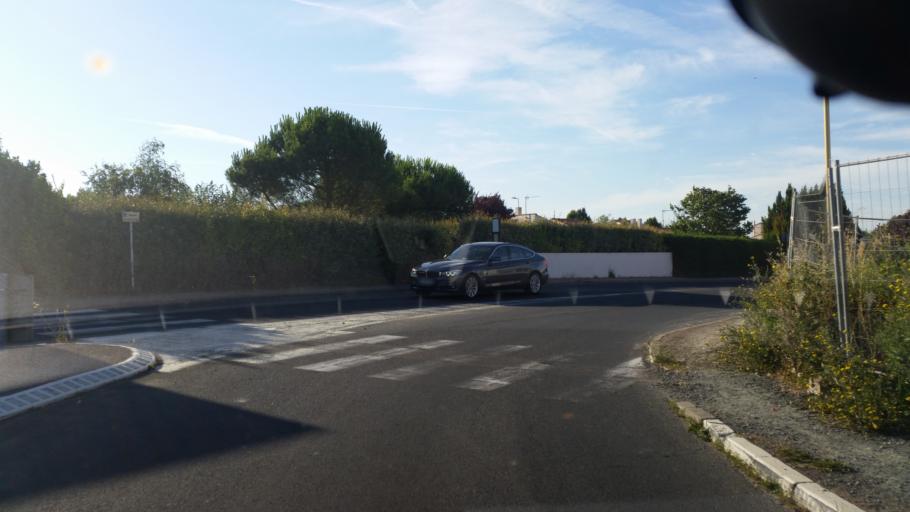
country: FR
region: Poitou-Charentes
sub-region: Departement de la Charente-Maritime
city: Puilboreau
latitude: 46.1715
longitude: -1.1075
